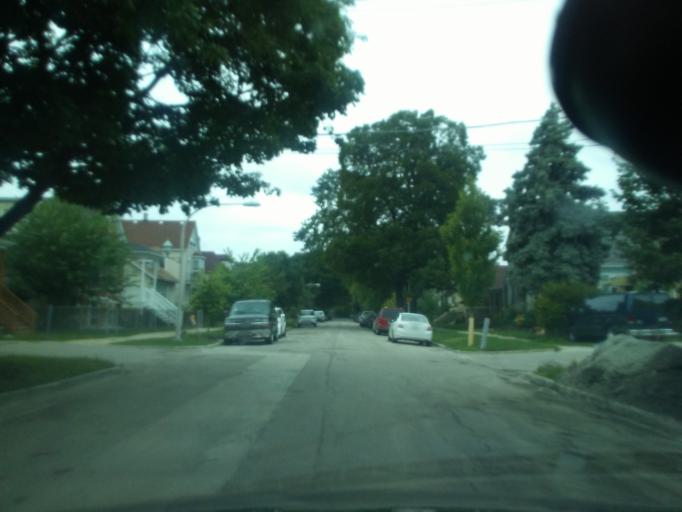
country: US
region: Illinois
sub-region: Cook County
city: Lincolnwood
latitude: 41.9707
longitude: -87.7450
